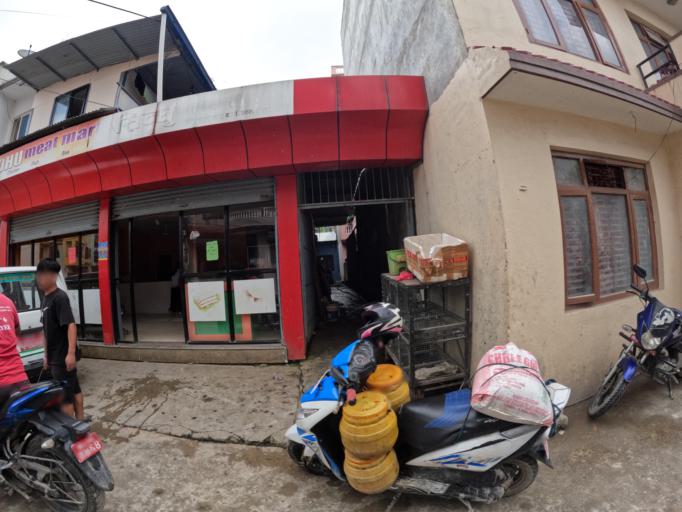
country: NP
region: Central Region
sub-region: Bagmati Zone
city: Kathmandu
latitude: 27.7454
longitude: 85.3201
